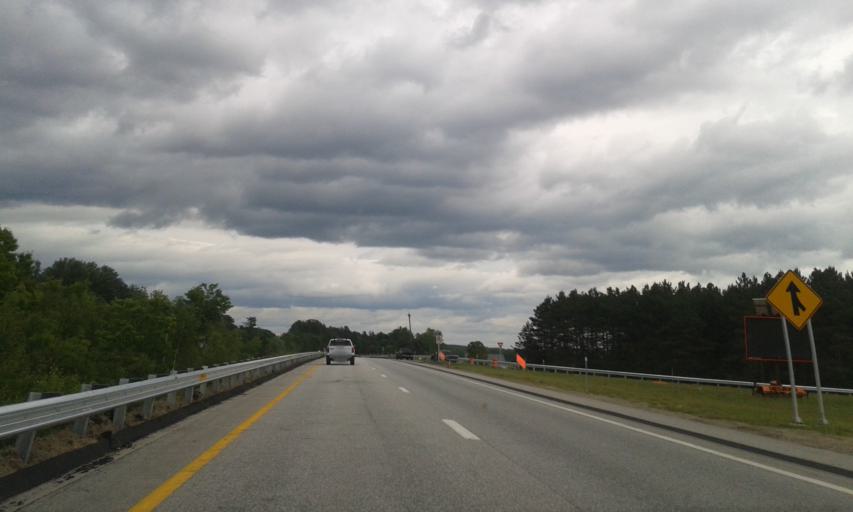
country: US
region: New Hampshire
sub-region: Merrimack County
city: Boscawen
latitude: 43.3323
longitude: -71.6074
